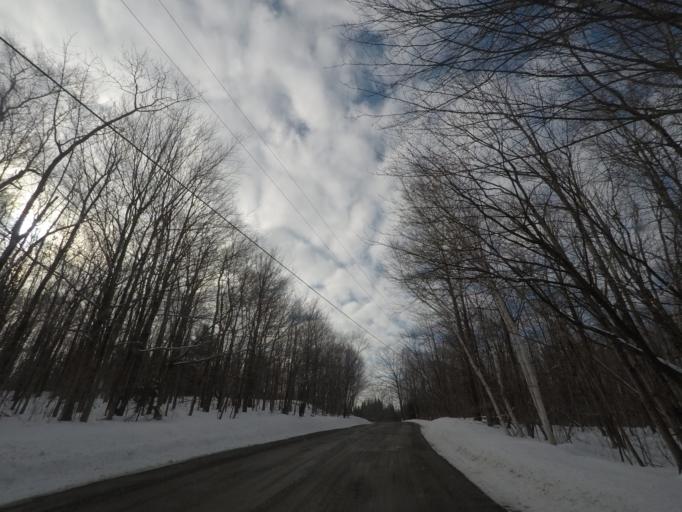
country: US
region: New York
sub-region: Rensselaer County
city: Averill Park
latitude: 42.6312
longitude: -73.4919
